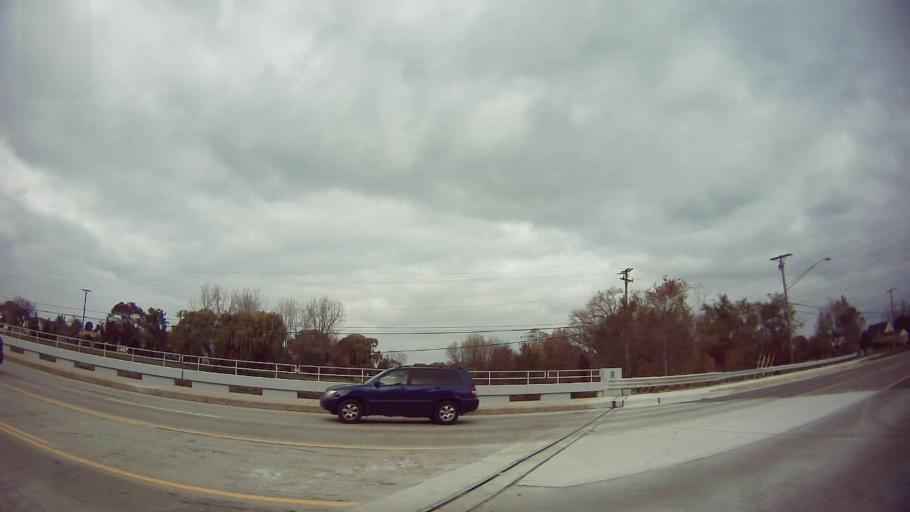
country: US
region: Michigan
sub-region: Macomb County
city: Fraser
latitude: 42.5523
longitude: -82.9858
